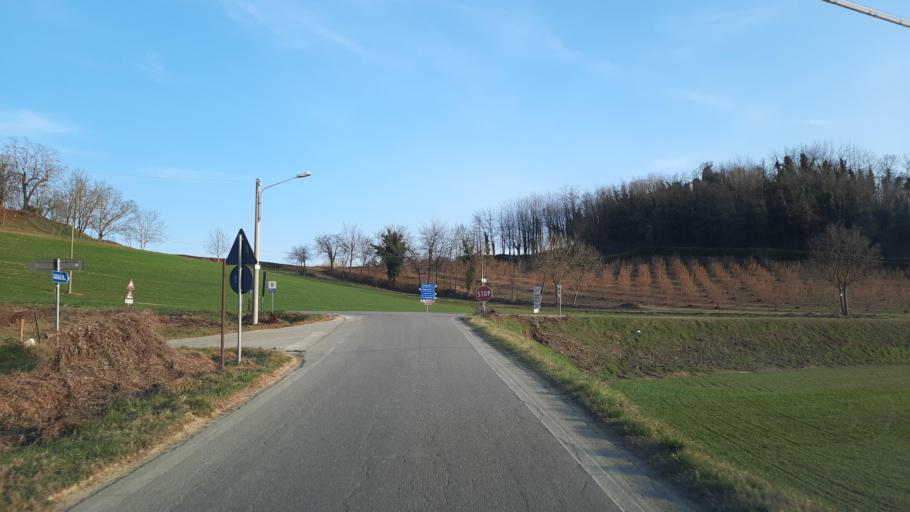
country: IT
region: Piedmont
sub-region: Provincia di Alessandria
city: Rosignano Monferrato
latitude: 45.0693
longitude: 8.4031
